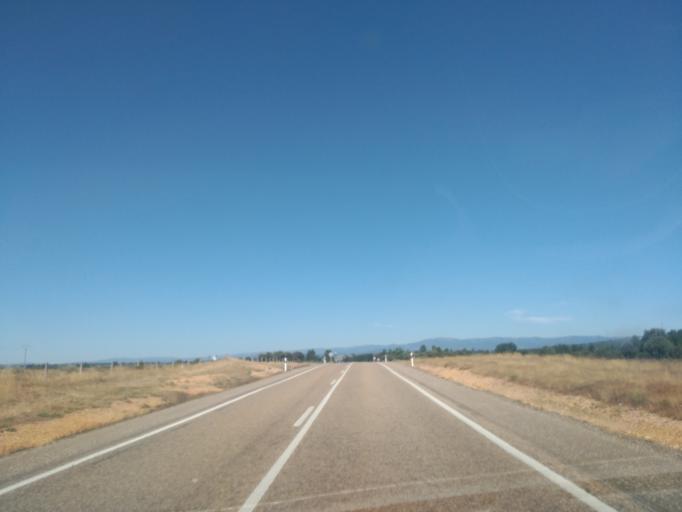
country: ES
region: Castille and Leon
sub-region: Provincia de Zamora
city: Otero de Bodas
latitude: 41.9472
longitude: -6.1939
